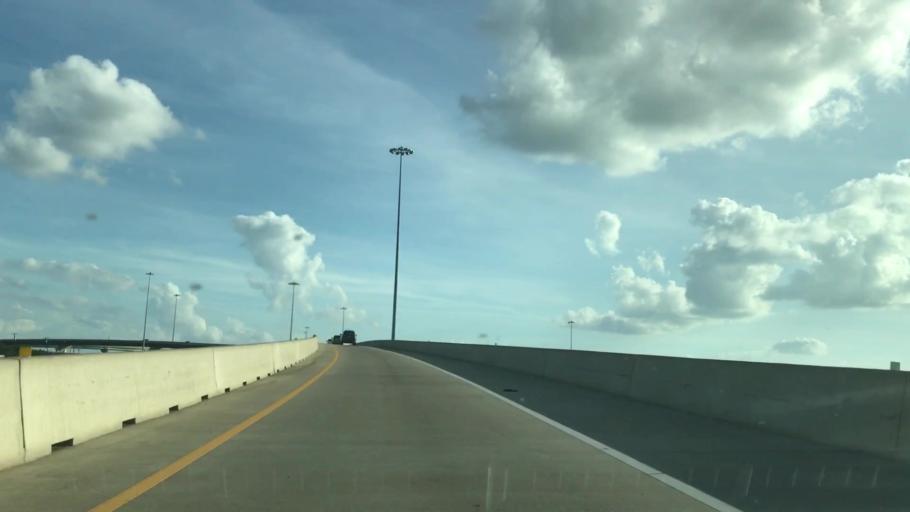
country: US
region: Texas
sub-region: Dallas County
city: Grand Prairie
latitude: 32.7648
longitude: -97.0297
